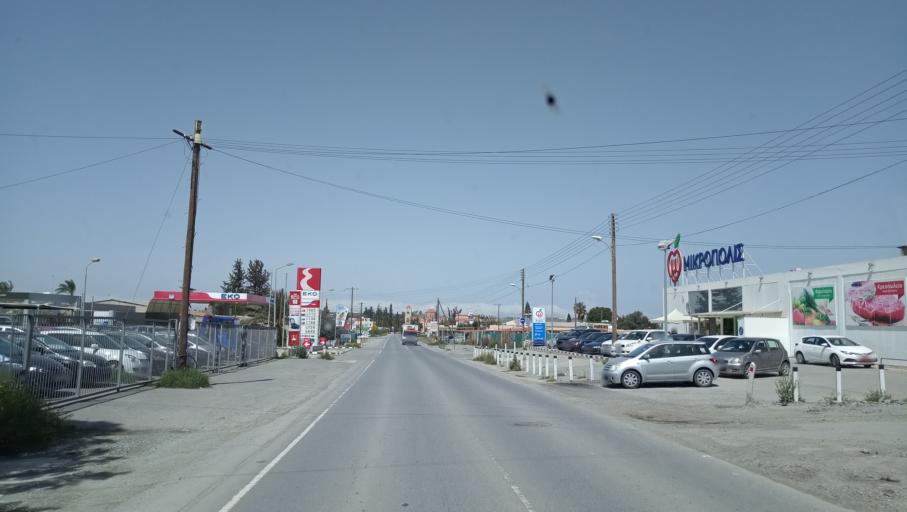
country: CY
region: Lefkosia
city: Alampra
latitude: 35.0082
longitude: 33.3939
